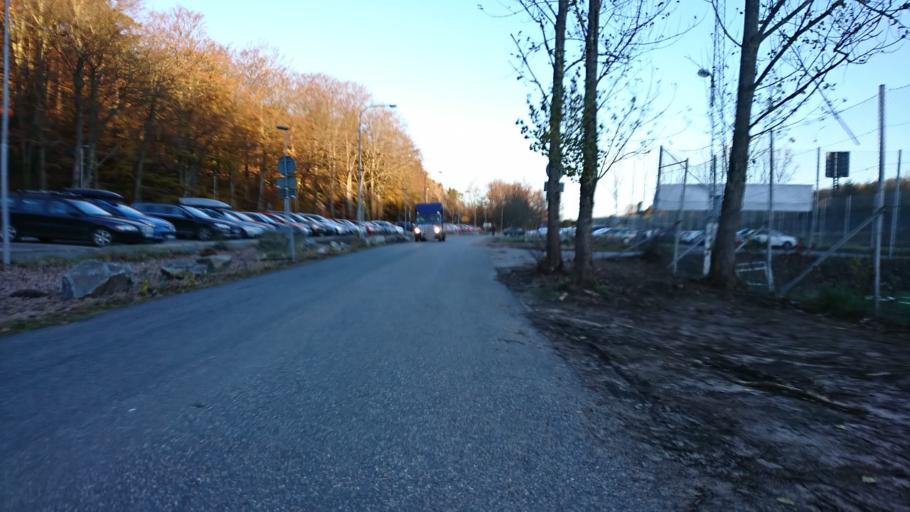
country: SE
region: Vaestra Goetaland
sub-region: Molndal
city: Moelndal
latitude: 57.6742
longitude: 12.0262
